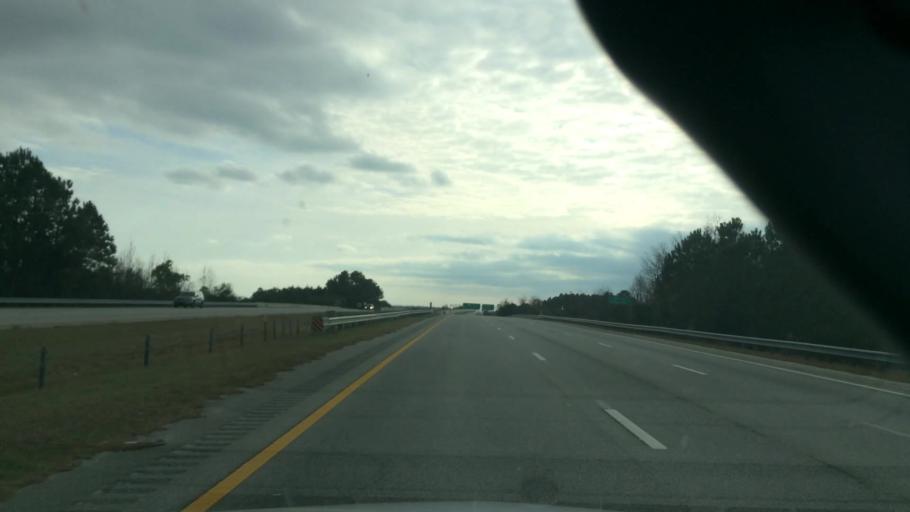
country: US
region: South Carolina
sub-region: Horry County
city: North Myrtle Beach
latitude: 33.8538
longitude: -78.6978
